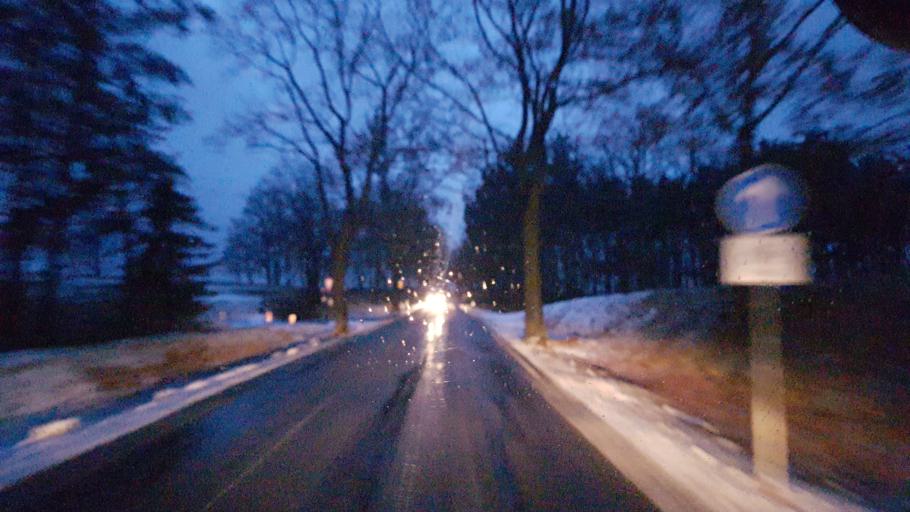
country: DE
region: Brandenburg
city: Werben
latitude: 51.7637
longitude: 14.1895
